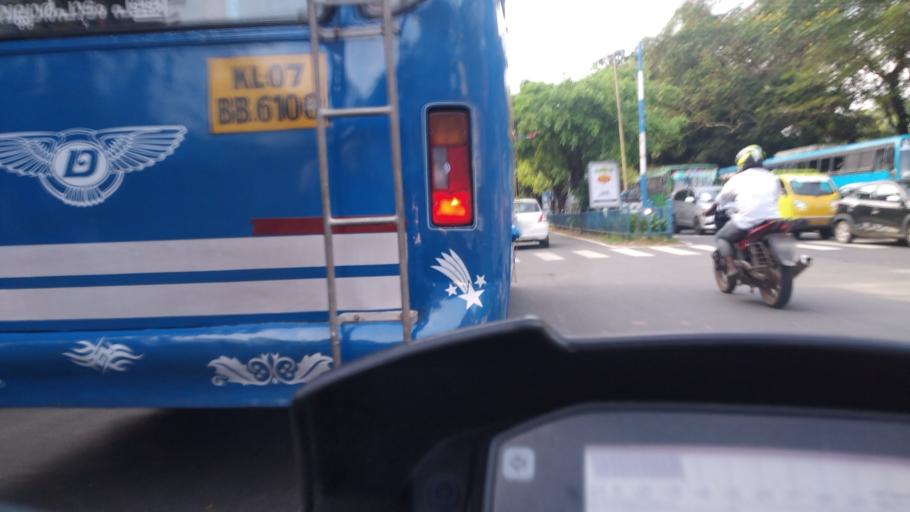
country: IN
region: Kerala
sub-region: Ernakulam
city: Cochin
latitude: 9.9848
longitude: 76.2735
